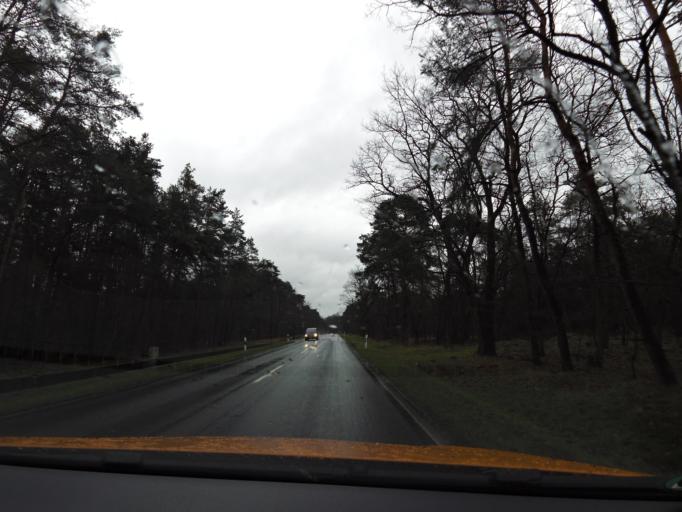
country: DE
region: Brandenburg
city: Am Mellensee
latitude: 52.1773
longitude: 13.3905
